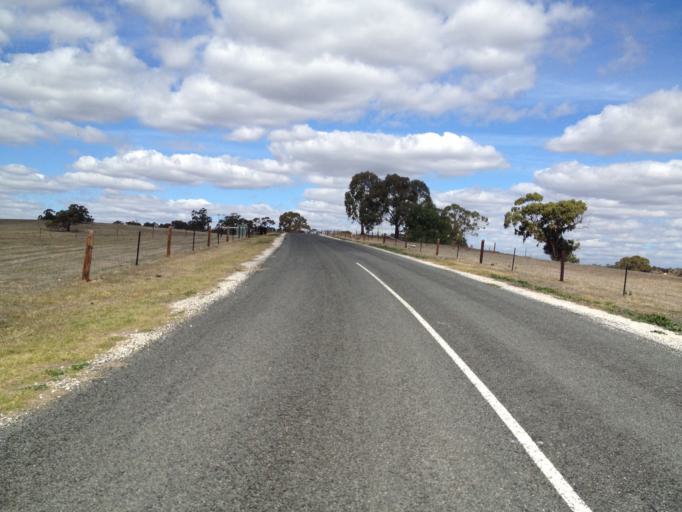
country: AU
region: South Australia
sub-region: Barossa
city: Lyndoch
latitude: -34.6298
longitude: 138.8308
